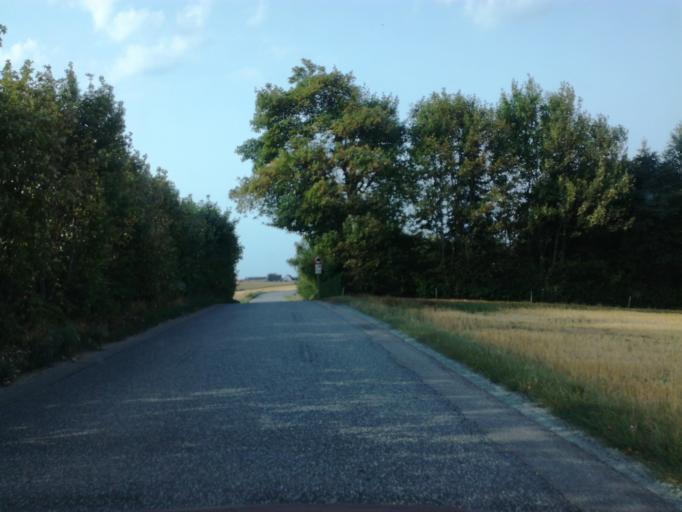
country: DK
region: South Denmark
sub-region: Vejle Kommune
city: Vejle
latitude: 55.6530
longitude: 9.5449
